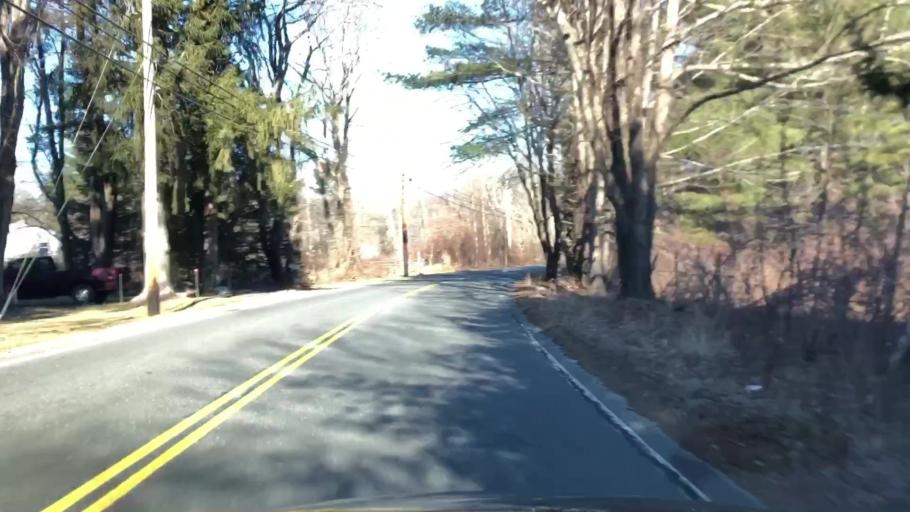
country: US
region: Massachusetts
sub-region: Worcester County
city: Charlton
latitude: 42.1094
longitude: -71.9720
